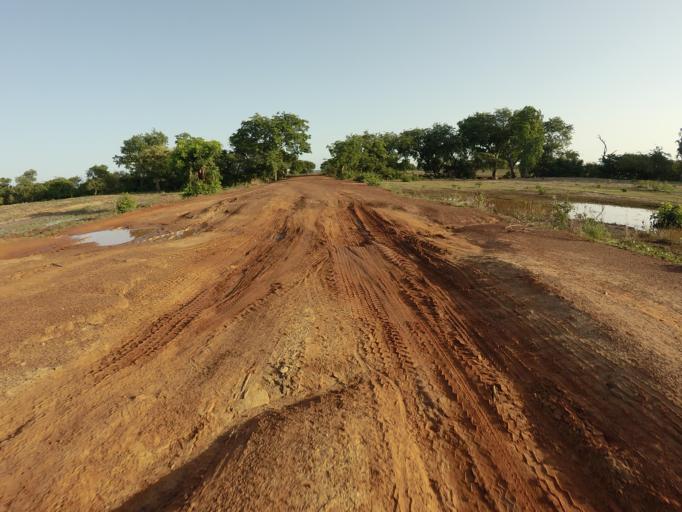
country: TG
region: Savanes
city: Sansanne-Mango
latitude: 10.3414
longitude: -0.0929
